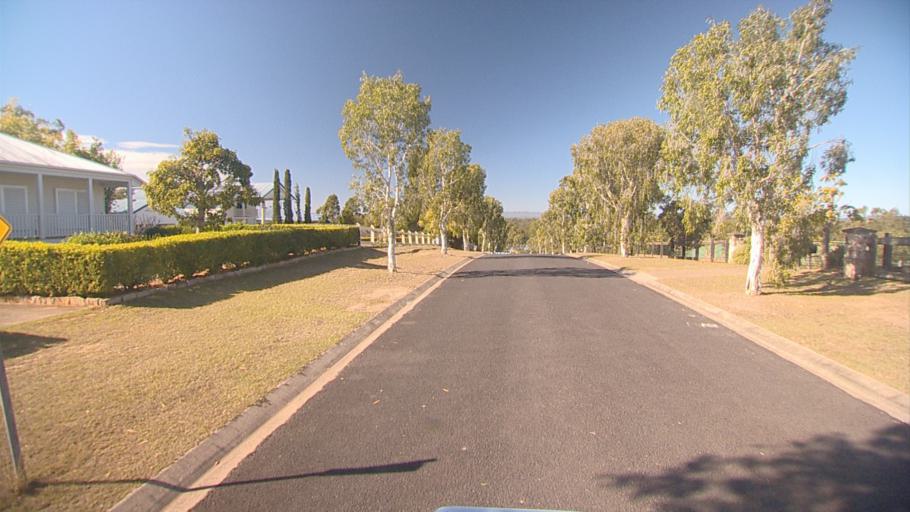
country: AU
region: Queensland
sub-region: Ipswich
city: Springfield Lakes
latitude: -27.7210
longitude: 152.9166
